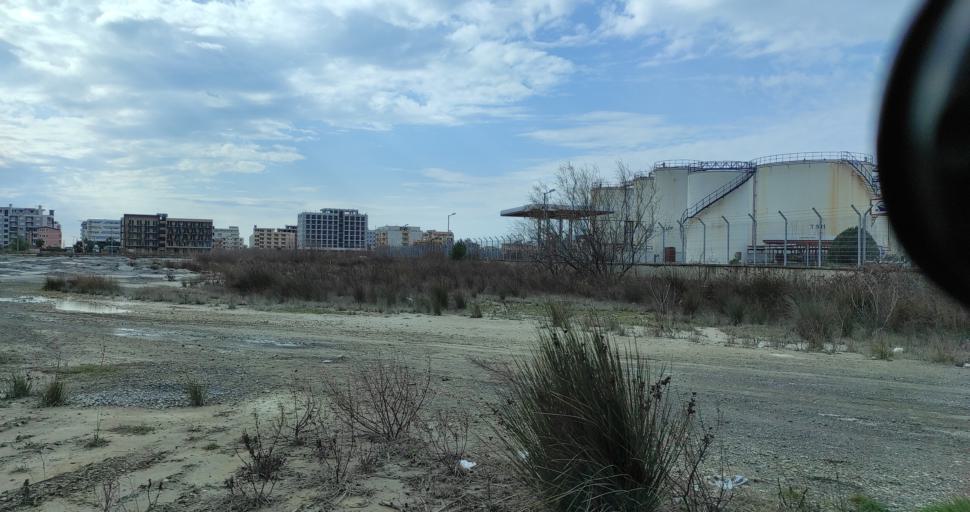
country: AL
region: Lezhe
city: Shengjin
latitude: 41.7969
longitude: 19.6101
